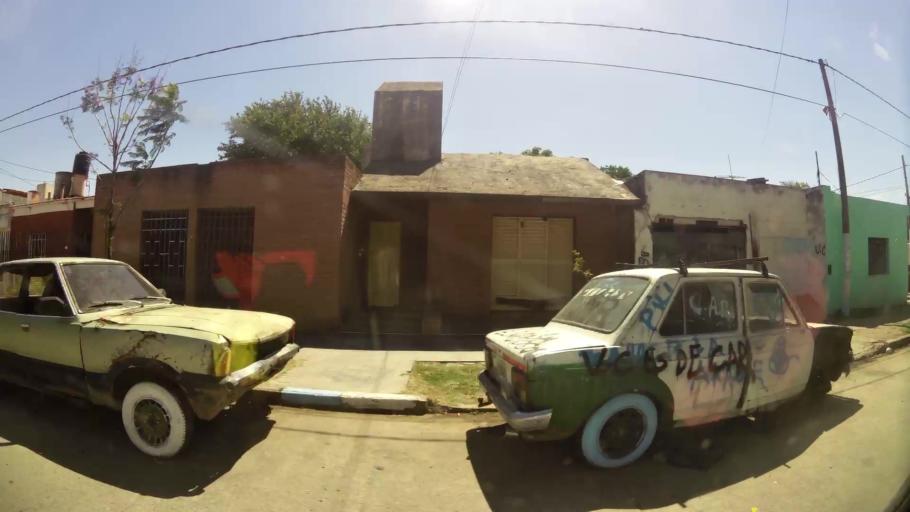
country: AR
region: Cordoba
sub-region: Departamento de Capital
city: Cordoba
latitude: -31.3723
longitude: -64.1430
